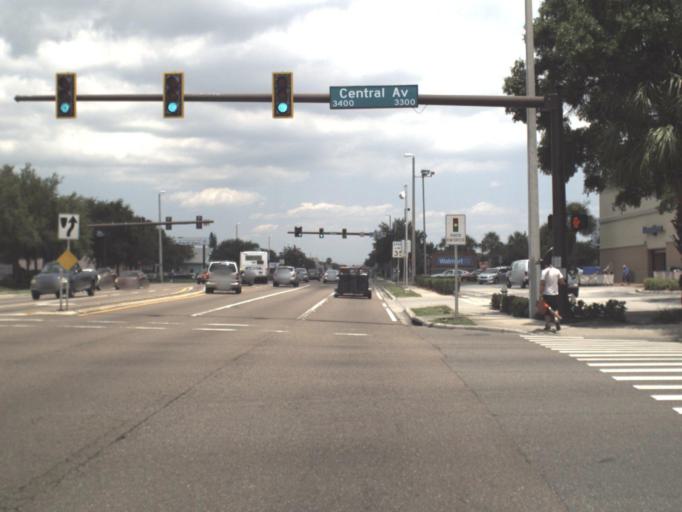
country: US
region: Florida
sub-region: Pinellas County
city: Saint Petersburg
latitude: 27.7709
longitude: -82.6793
